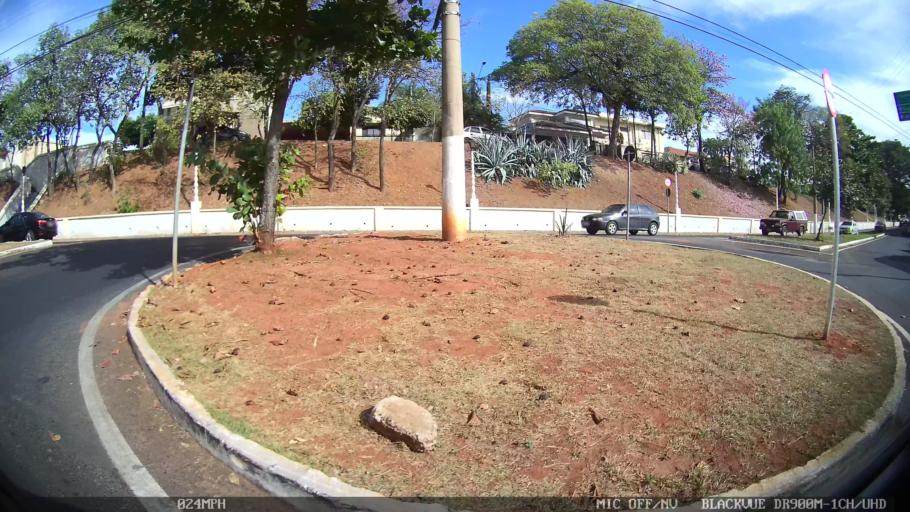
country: BR
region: Sao Paulo
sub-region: Catanduva
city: Catanduva
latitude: -21.1289
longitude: -48.9810
